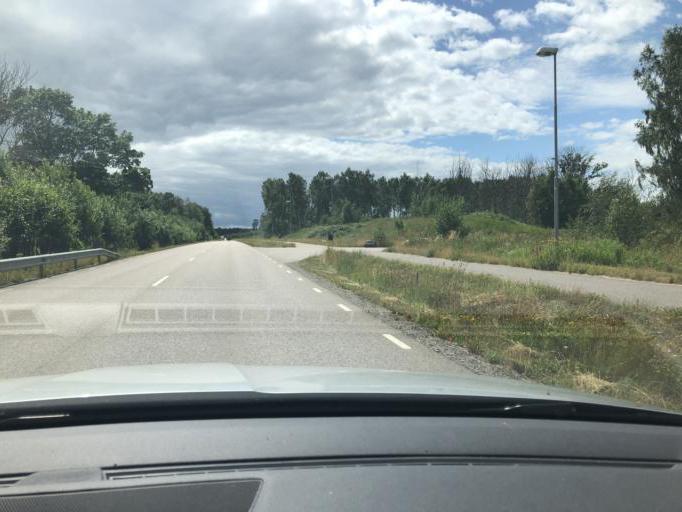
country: SE
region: Blekinge
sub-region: Solvesborgs Kommun
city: Soelvesborg
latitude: 56.0540
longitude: 14.6152
